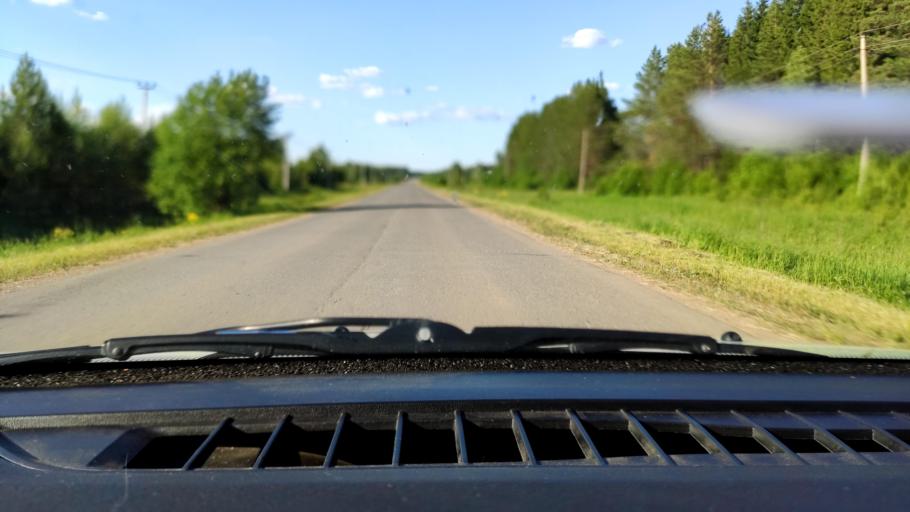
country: RU
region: Perm
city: Uinskoye
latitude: 57.1069
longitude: 56.6604
